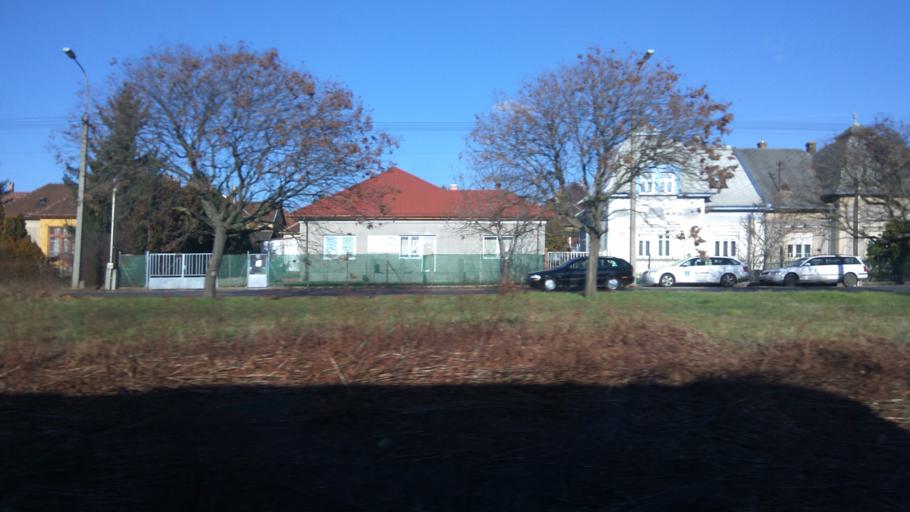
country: HU
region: Budapest
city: Budapest XVII. keruelet
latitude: 47.4868
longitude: 19.2529
